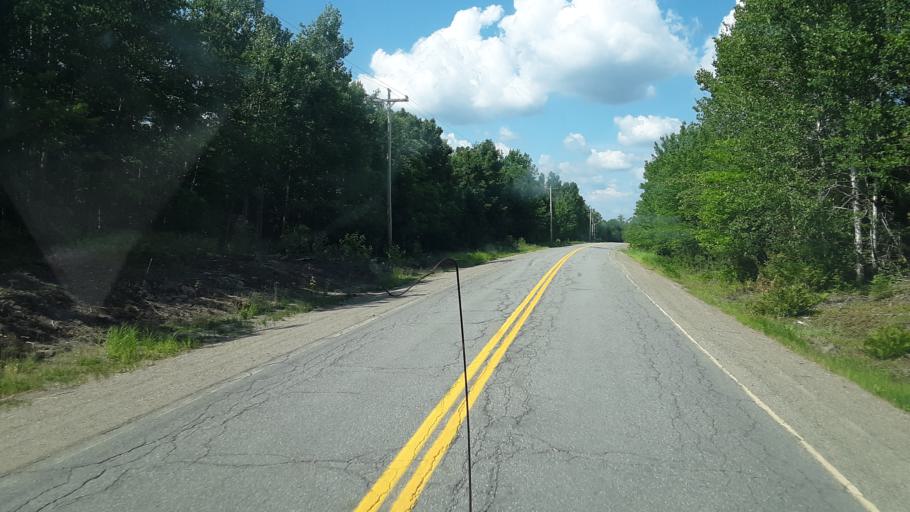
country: US
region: Maine
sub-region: Washington County
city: Calais
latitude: 45.1096
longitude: -67.5078
